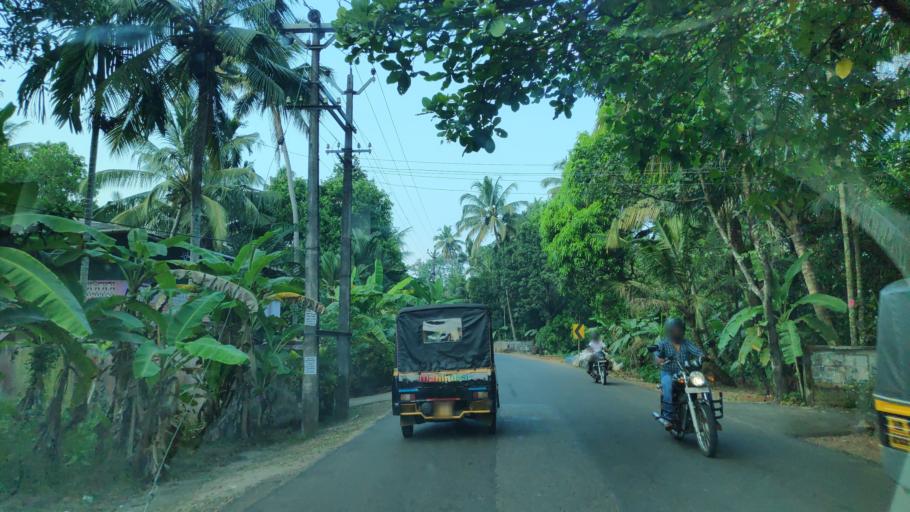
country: IN
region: Kerala
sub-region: Alappuzha
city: Shertallai
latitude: 9.6724
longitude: 76.3898
